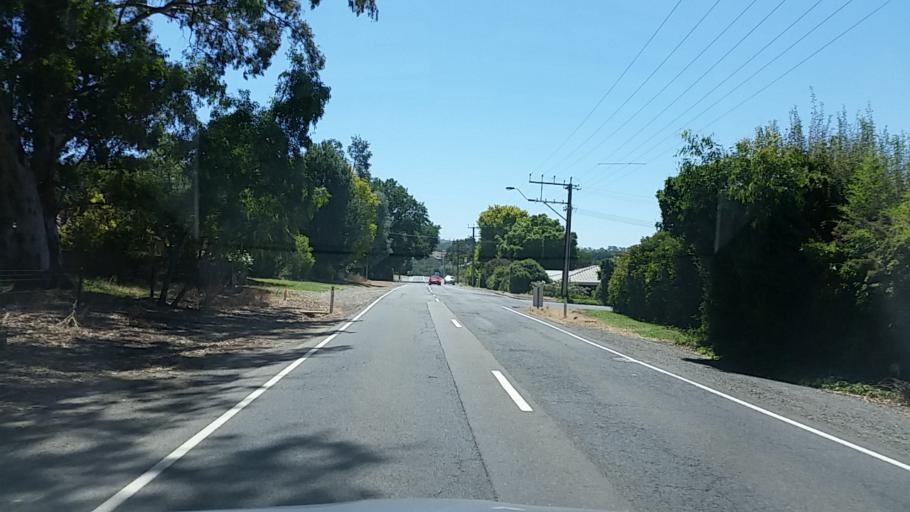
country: AU
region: South Australia
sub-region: Adelaide Hills
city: Balhannah
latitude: -34.9942
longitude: 138.8288
